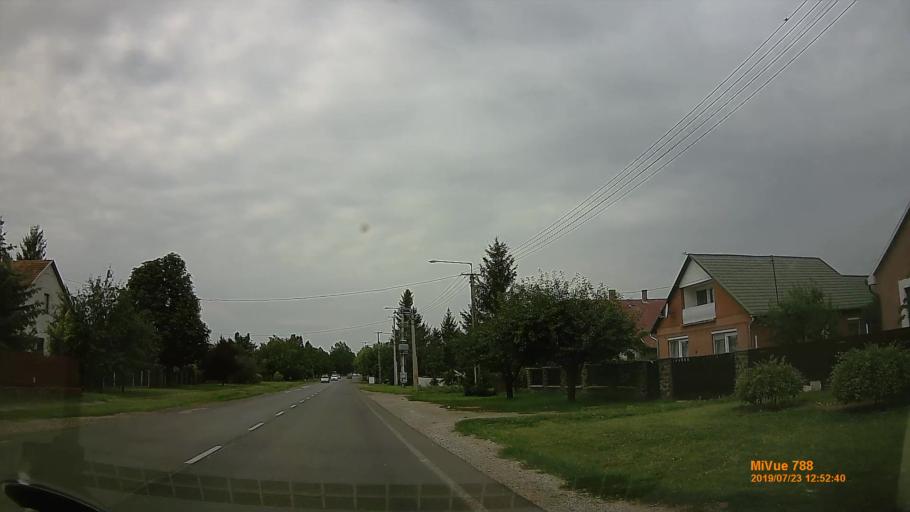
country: HU
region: Szabolcs-Szatmar-Bereg
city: Nagycserkesz
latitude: 47.9620
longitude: 21.5638
